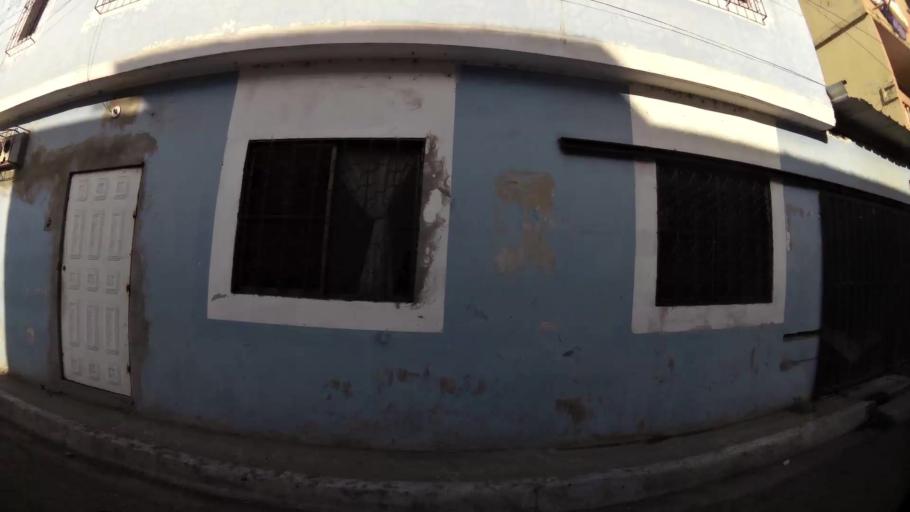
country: EC
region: Guayas
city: Guayaquil
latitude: -2.2254
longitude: -79.9093
